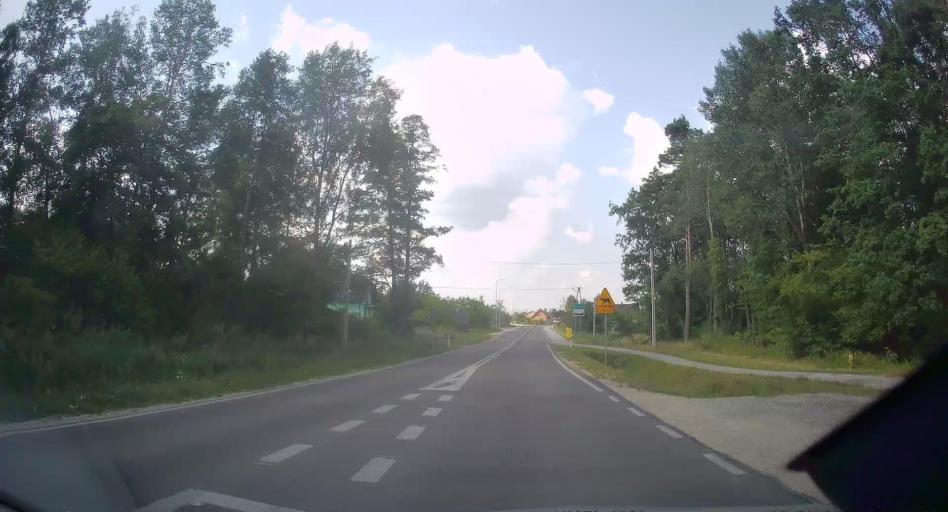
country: PL
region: Swietokrzyskie
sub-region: Powiat konecki
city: Radoszyce
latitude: 51.0248
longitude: 20.2906
